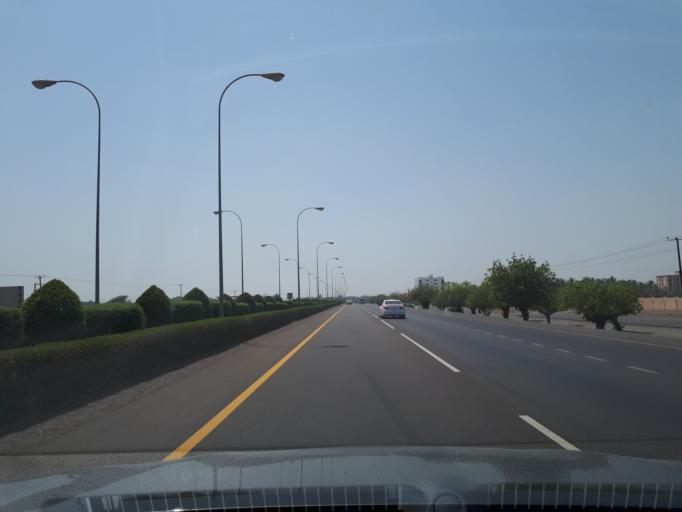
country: OM
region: Al Batinah
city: Al Sohar
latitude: 24.4073
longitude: 56.6509
